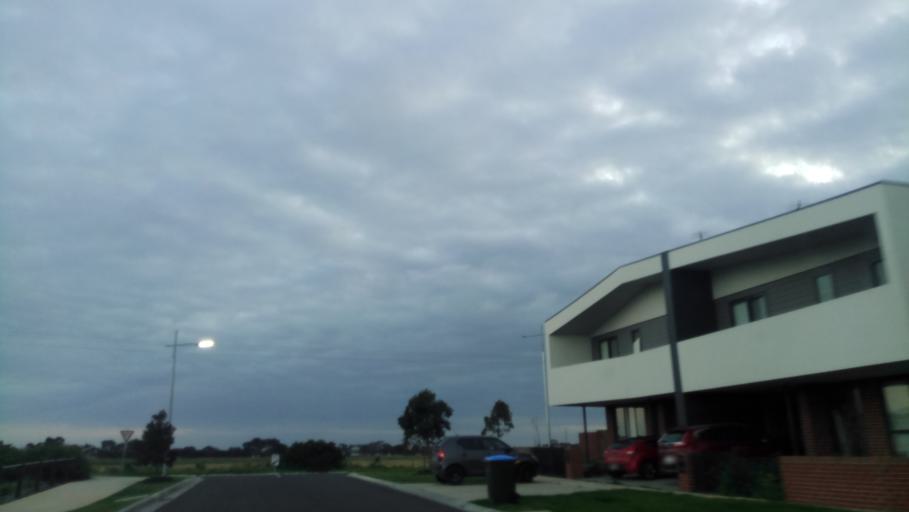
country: AU
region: Victoria
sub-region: Wyndham
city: Point Cook
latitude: -37.9151
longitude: 144.7600
